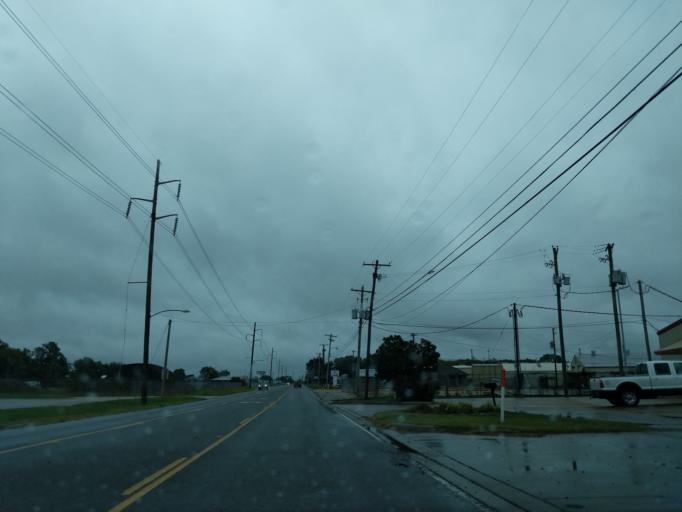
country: US
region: Louisiana
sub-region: Bossier Parish
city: Bossier City
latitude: 32.5241
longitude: -93.6860
